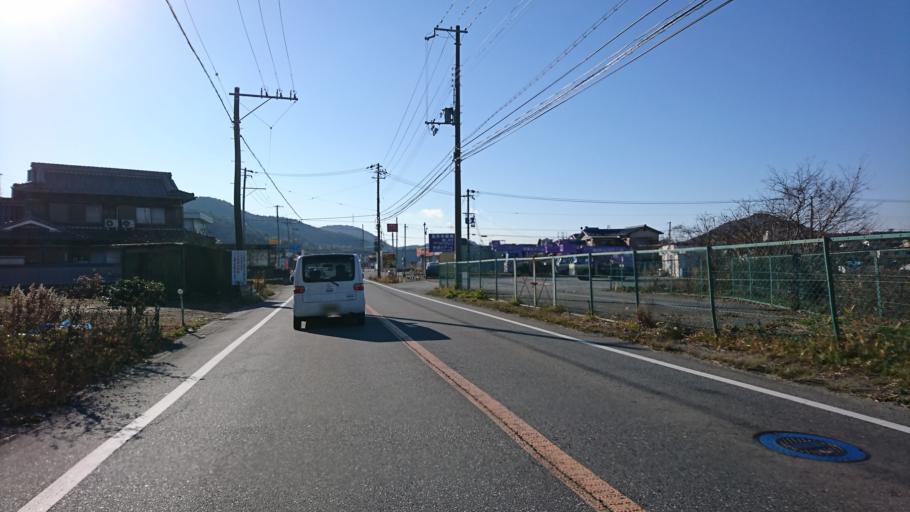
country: JP
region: Hyogo
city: Kakogawacho-honmachi
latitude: 34.8165
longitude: 134.8352
